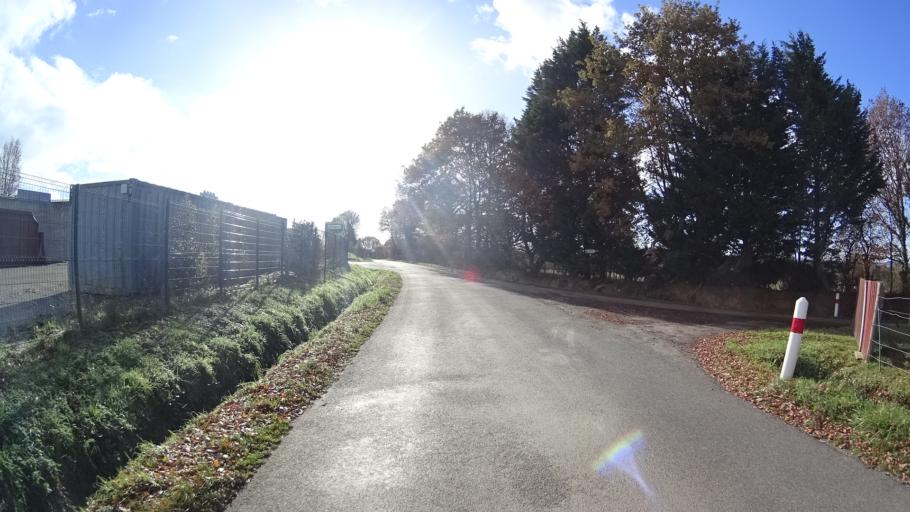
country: FR
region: Brittany
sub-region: Departement du Morbihan
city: Carentoir
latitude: 47.8055
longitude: -2.1403
